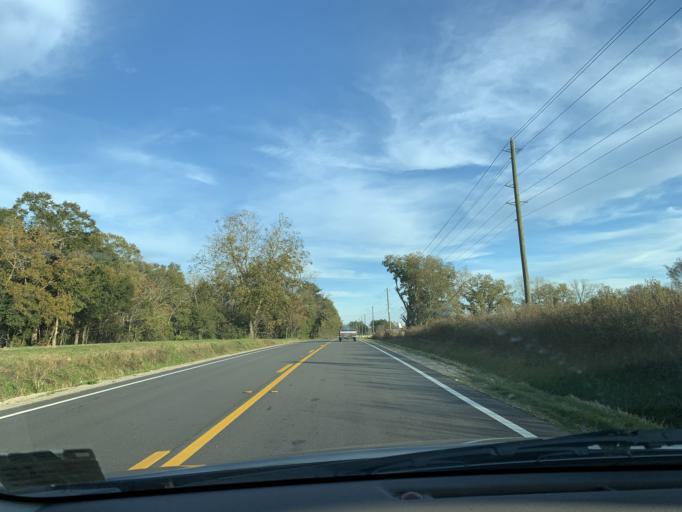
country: US
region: Georgia
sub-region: Irwin County
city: Ocilla
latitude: 31.5924
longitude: -83.1024
